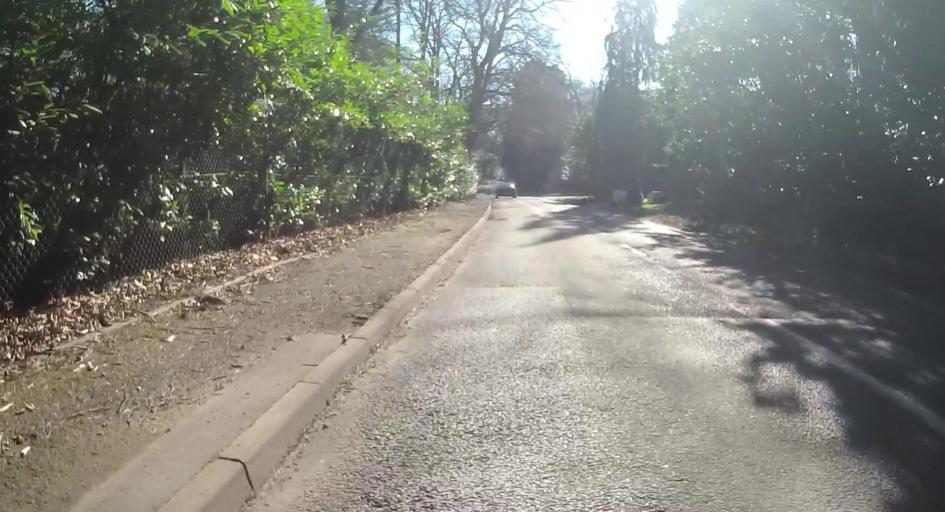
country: GB
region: England
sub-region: Royal Borough of Windsor and Maidenhead
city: Ascot
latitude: 51.3911
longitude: -0.6657
